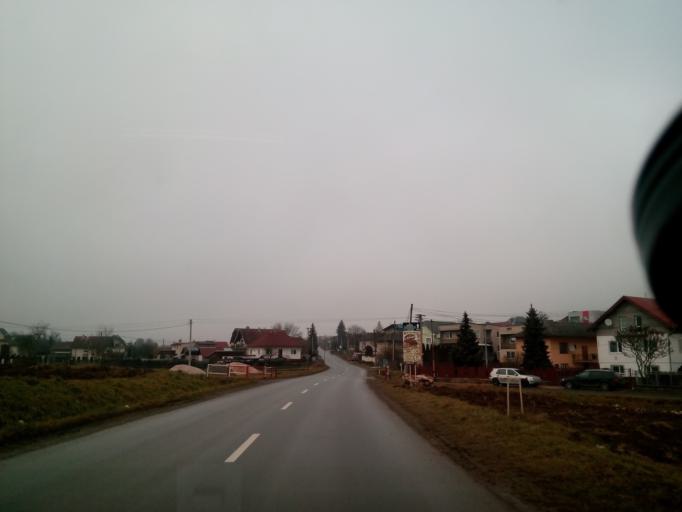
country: SK
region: Kosicky
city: Krompachy
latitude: 48.9649
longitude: 20.9555
